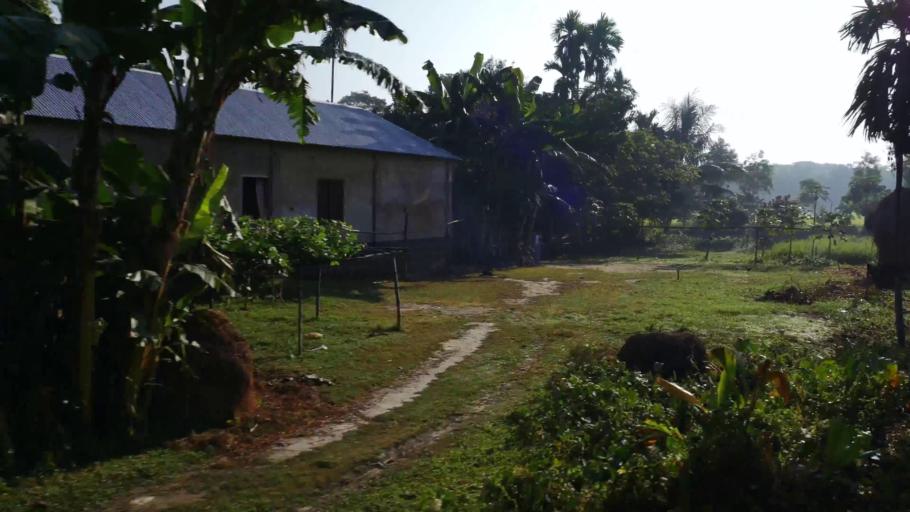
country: BD
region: Dhaka
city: Jamalpur
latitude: 24.8638
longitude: 90.0598
